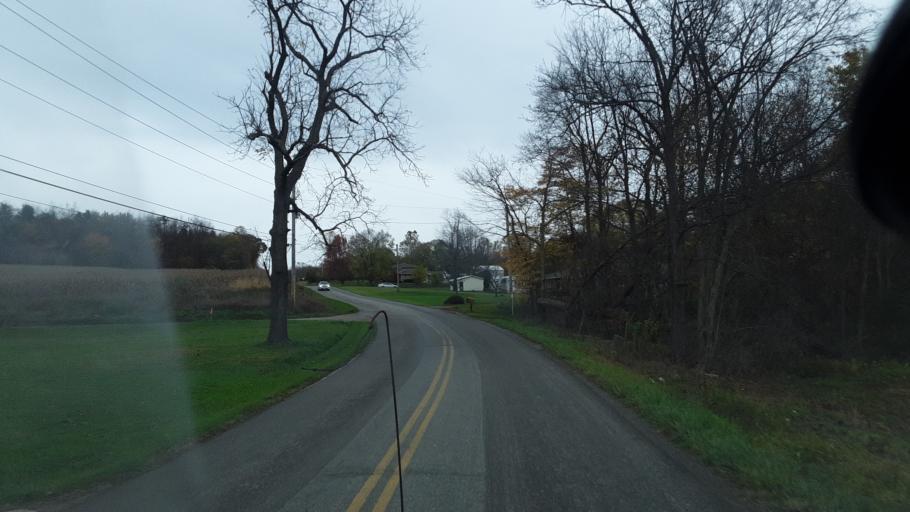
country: US
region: Ohio
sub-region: Holmes County
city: Millersburg
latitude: 40.4858
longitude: -81.9283
